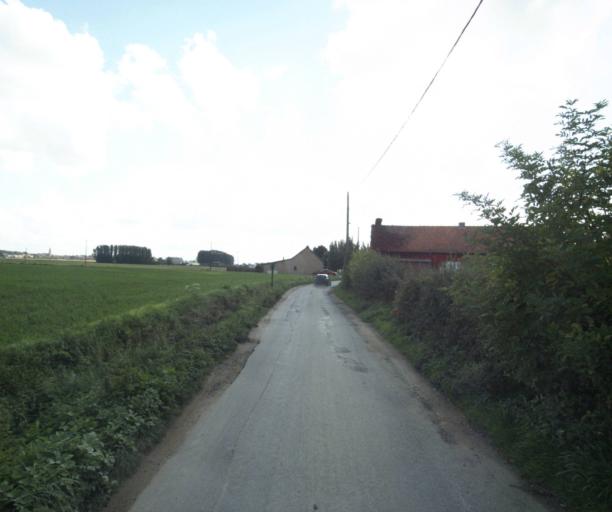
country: FR
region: Nord-Pas-de-Calais
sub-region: Departement du Pas-de-Calais
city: Lorgies
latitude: 50.5693
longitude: 2.8107
